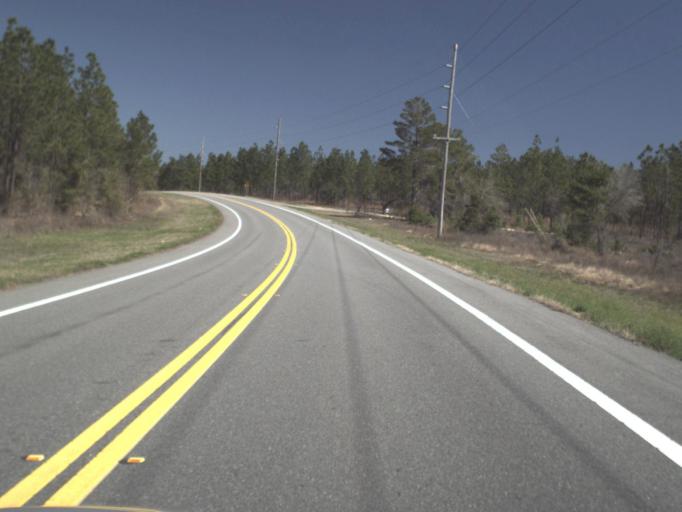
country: US
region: Florida
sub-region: Gadsden County
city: Quincy
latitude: 30.4179
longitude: -84.6516
